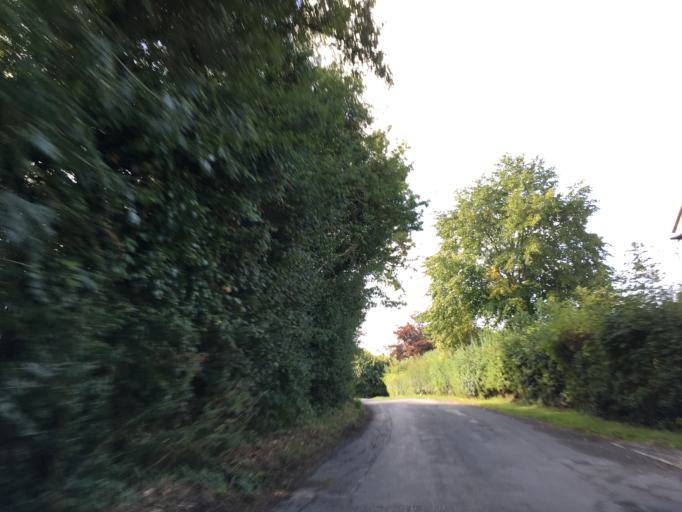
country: GB
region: England
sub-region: South Gloucestershire
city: Horton
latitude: 51.5271
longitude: -2.3592
